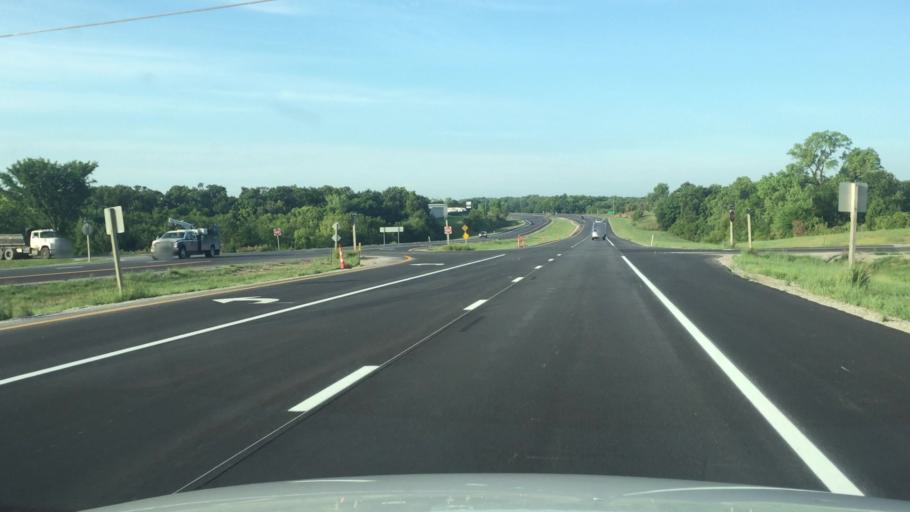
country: US
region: Kansas
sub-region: Johnson County
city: Spring Hill
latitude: 38.7578
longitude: -94.8355
